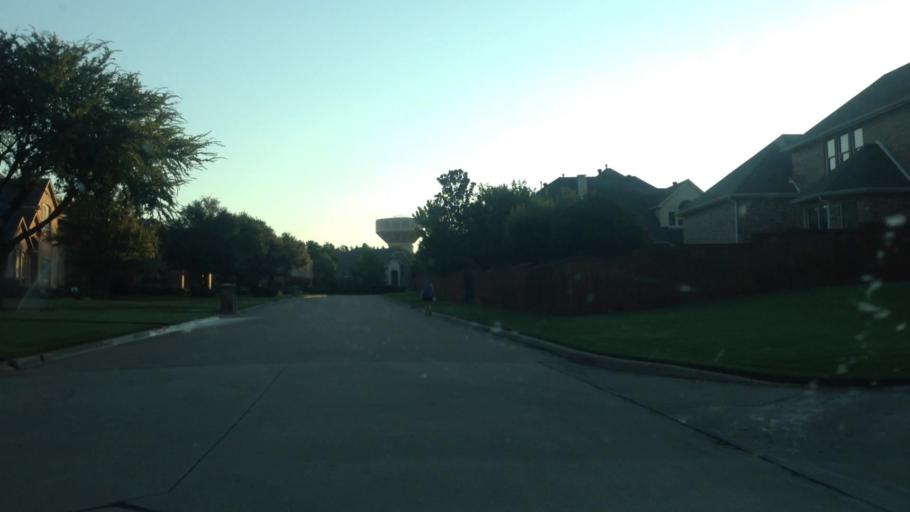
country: US
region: Texas
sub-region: Tarrant County
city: Southlake
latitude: 32.9357
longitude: -97.1316
